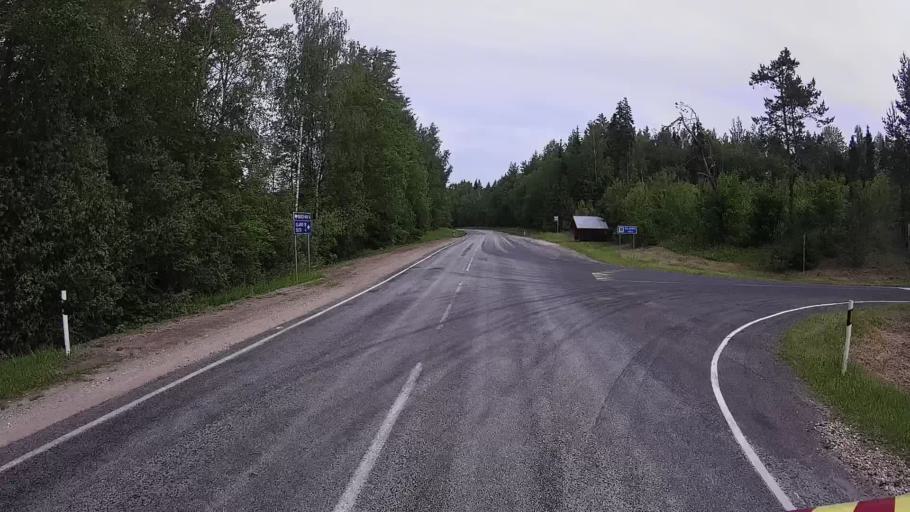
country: EE
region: Viljandimaa
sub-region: Karksi vald
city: Karksi-Nuia
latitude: 58.2085
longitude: 25.6211
